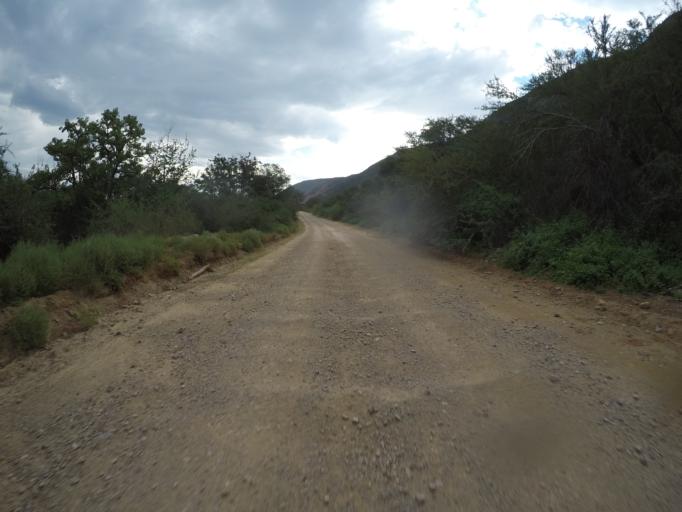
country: ZA
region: Eastern Cape
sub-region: Cacadu District Municipality
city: Kareedouw
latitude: -33.5757
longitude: 24.1412
